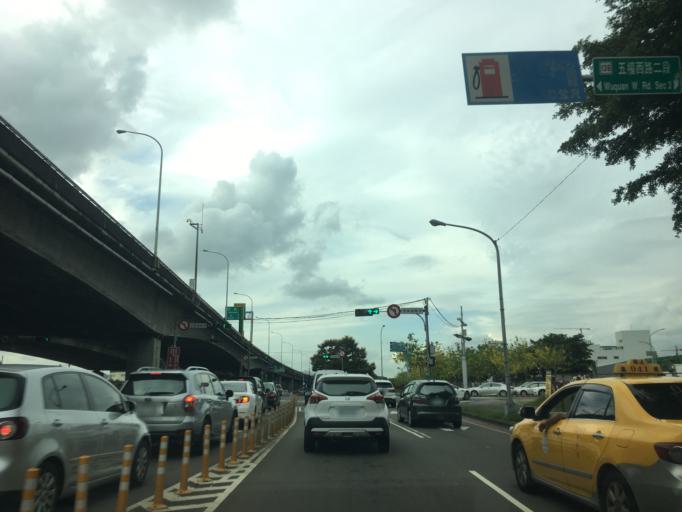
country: TW
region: Taiwan
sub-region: Taichung City
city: Taichung
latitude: 24.1489
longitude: 120.6236
